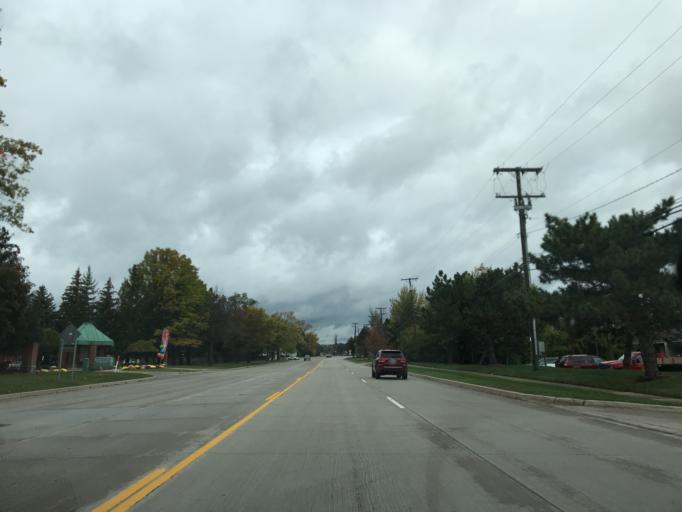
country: US
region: Michigan
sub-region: Oakland County
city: Franklin
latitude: 42.4952
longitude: -83.3018
